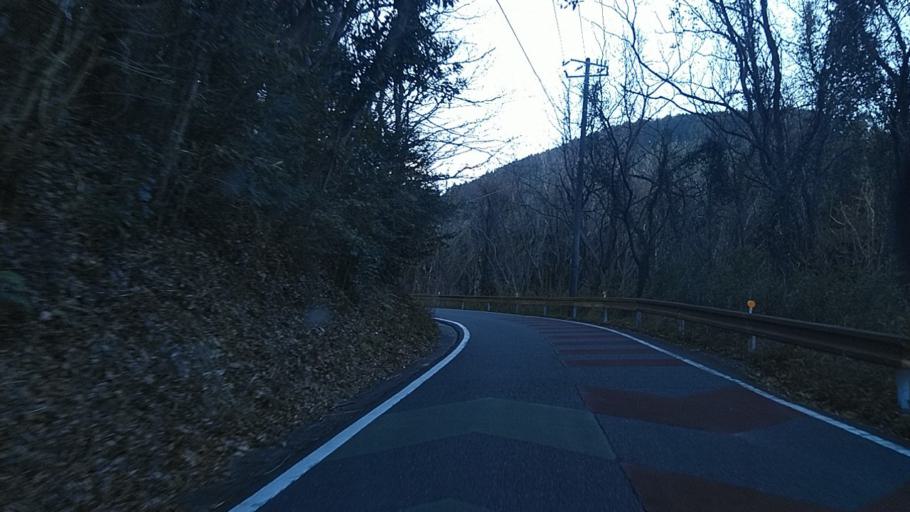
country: JP
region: Chiba
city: Kimitsu
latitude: 35.2611
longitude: 139.9433
